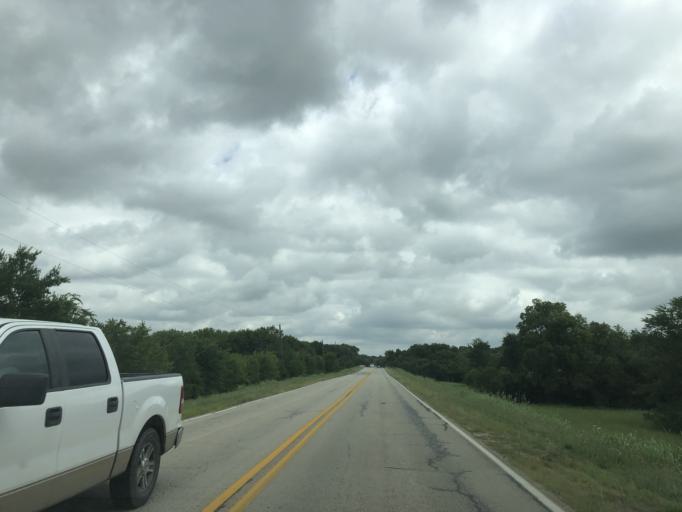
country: US
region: Texas
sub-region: Dallas County
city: Sunnyvale
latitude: 32.8154
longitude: -96.5596
